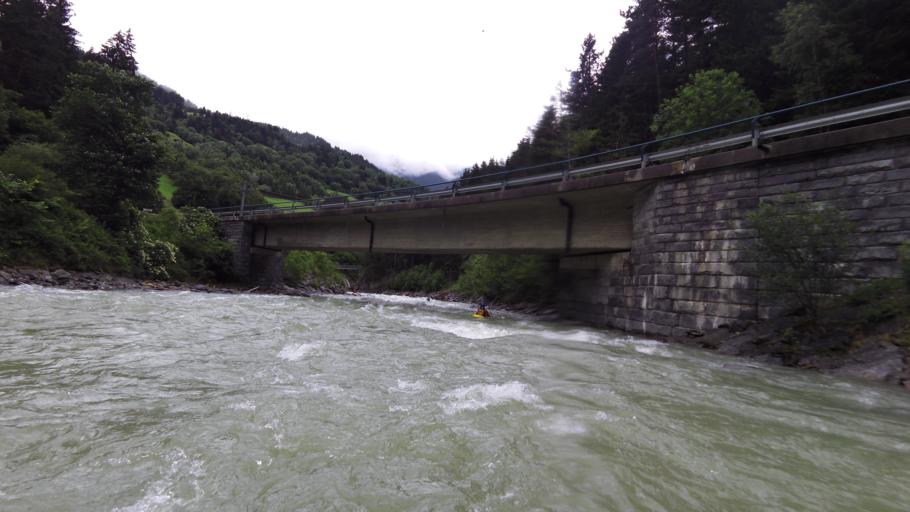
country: AT
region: Tyrol
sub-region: Politischer Bezirk Landeck
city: Pians
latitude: 47.1261
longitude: 10.4985
